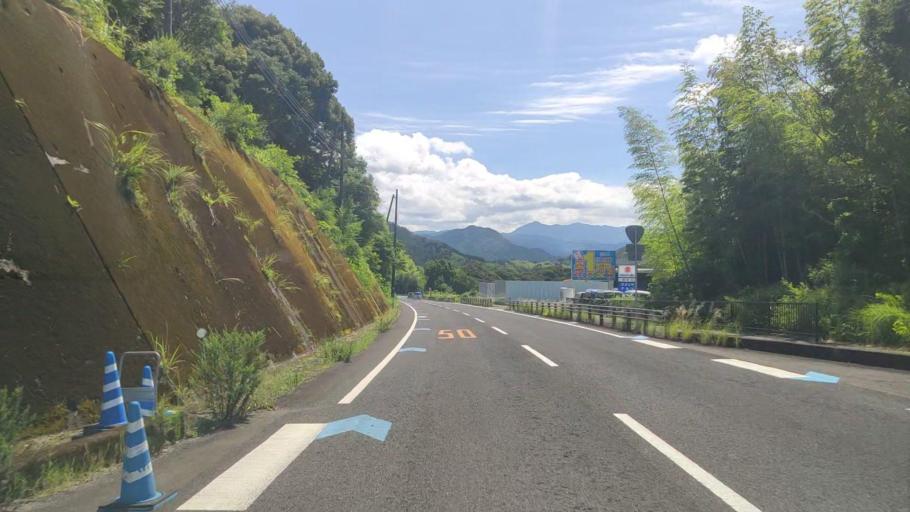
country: JP
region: Wakayama
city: Shingu
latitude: 33.7443
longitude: 136.0095
